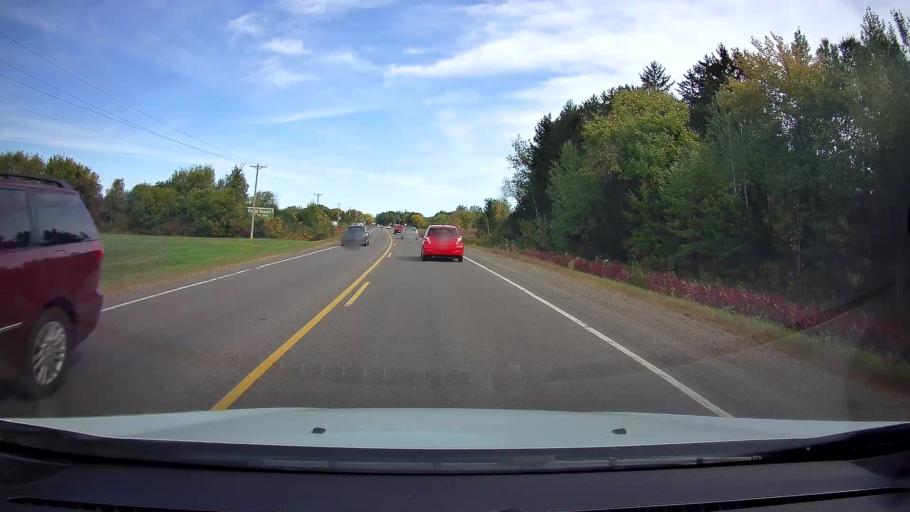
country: US
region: Wisconsin
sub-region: Polk County
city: Saint Croix Falls
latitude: 45.3457
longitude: -92.6410
